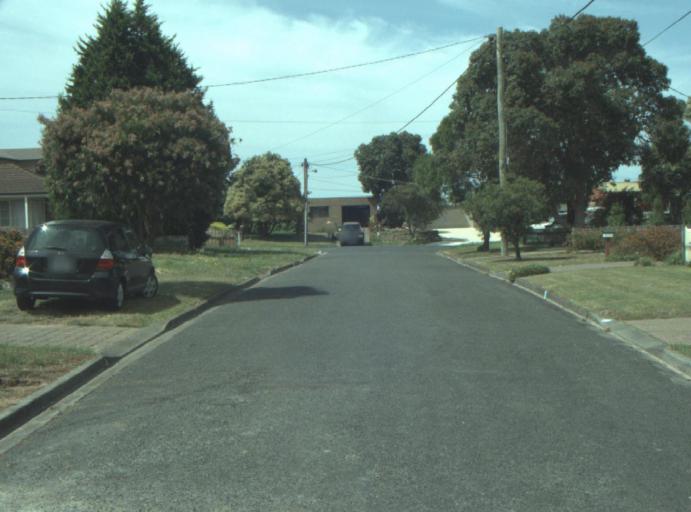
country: AU
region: Victoria
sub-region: Greater Geelong
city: Clifton Springs
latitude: -38.1635
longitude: 144.5650
